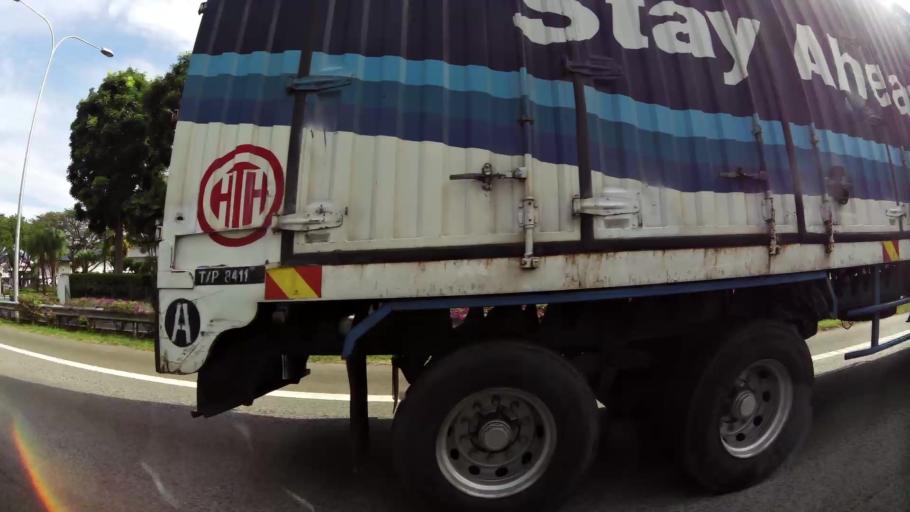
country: MY
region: Johor
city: Johor Bahru
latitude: 1.3339
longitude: 103.6521
